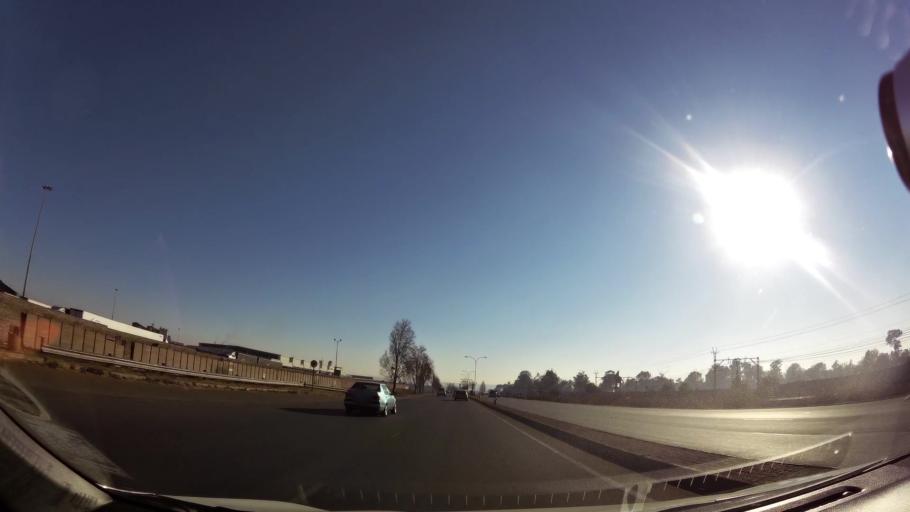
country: ZA
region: Gauteng
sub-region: Ekurhuleni Metropolitan Municipality
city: Germiston
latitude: -26.3218
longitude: 28.1394
